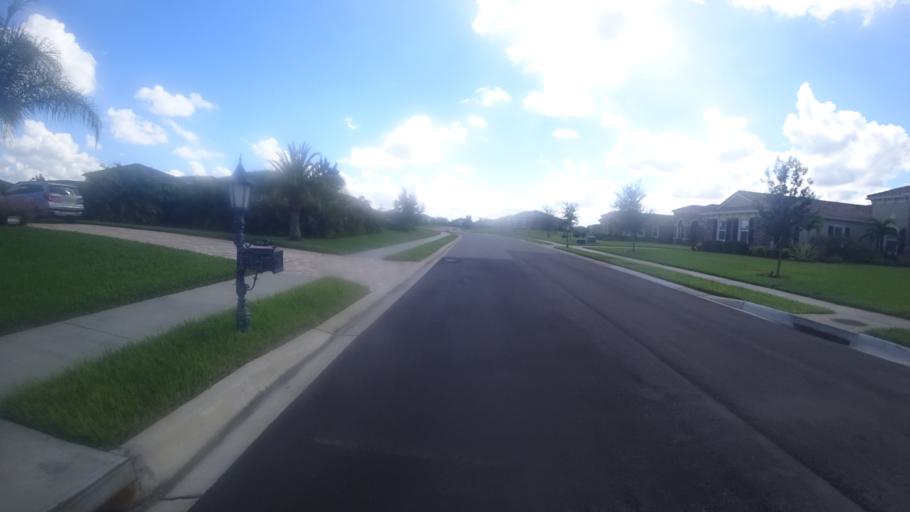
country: US
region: Florida
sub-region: Manatee County
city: Ellenton
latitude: 27.4952
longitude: -82.3721
